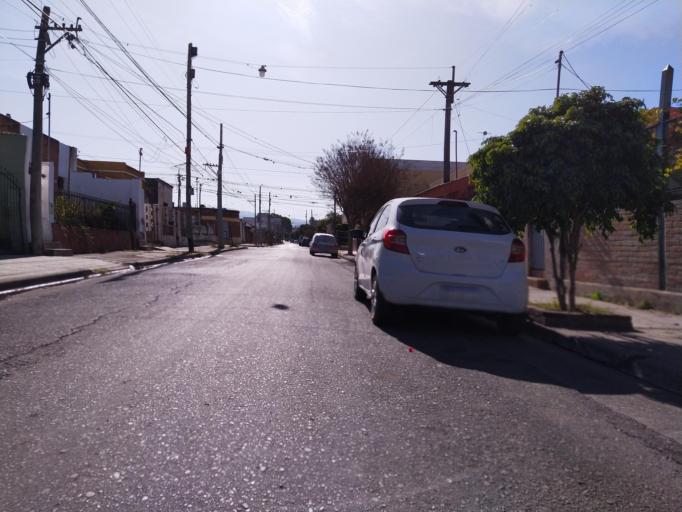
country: AR
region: Jujuy
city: San Salvador de Jujuy
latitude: -24.2013
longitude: -65.2860
